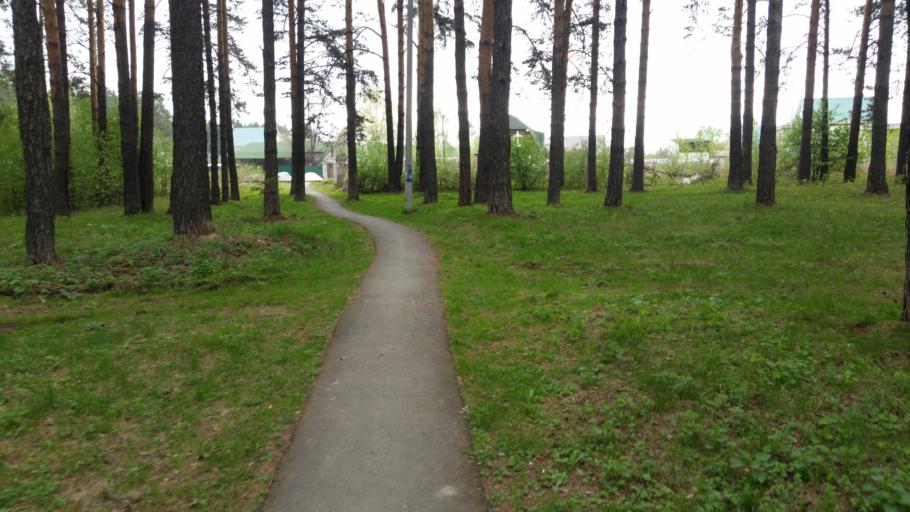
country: RU
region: Sverdlovsk
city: Beryozovsky
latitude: 56.9029
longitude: 60.7647
